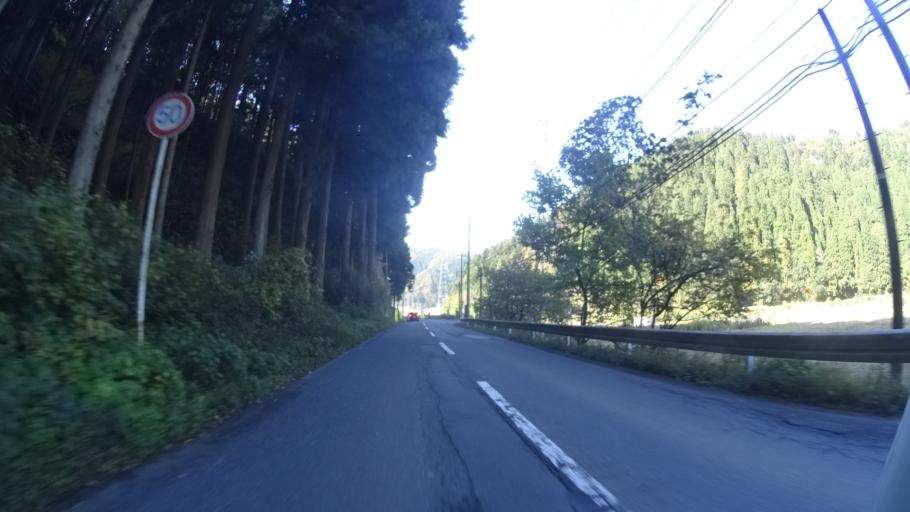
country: JP
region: Fukui
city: Ono
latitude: 35.9827
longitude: 136.3692
